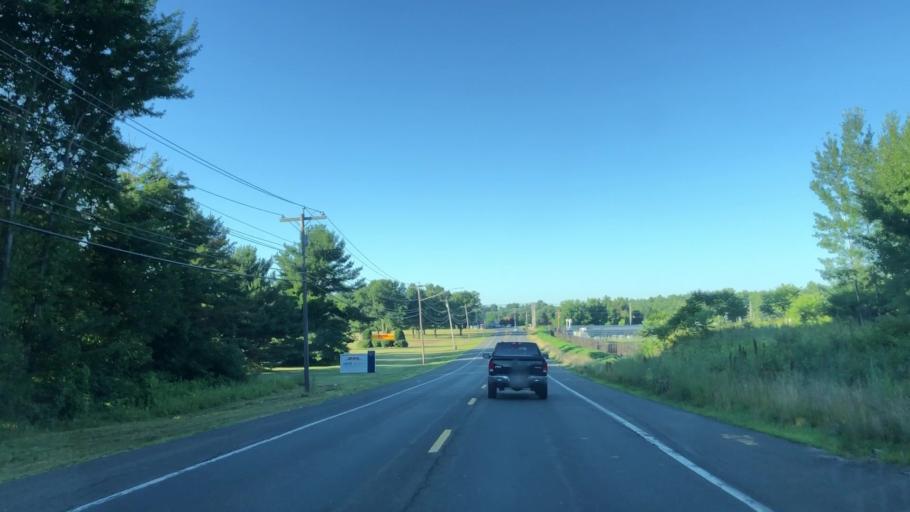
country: US
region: Massachusetts
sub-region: Hampshire County
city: Southampton
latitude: 42.1794
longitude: -72.7268
